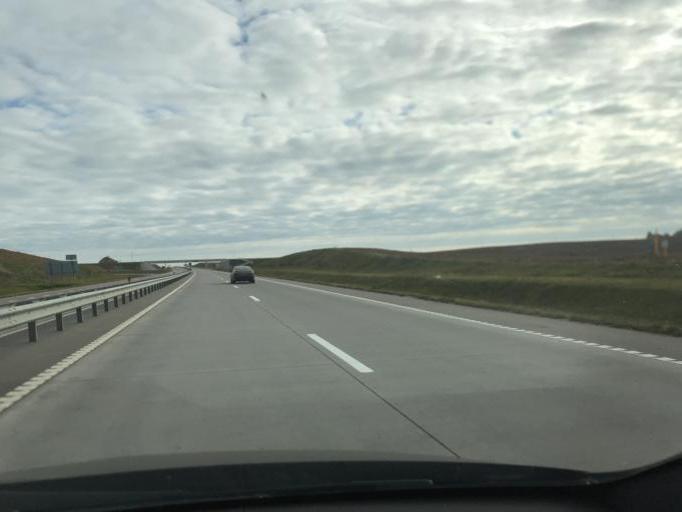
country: BY
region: Minsk
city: Syomkava
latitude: 54.0647
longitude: 27.4938
